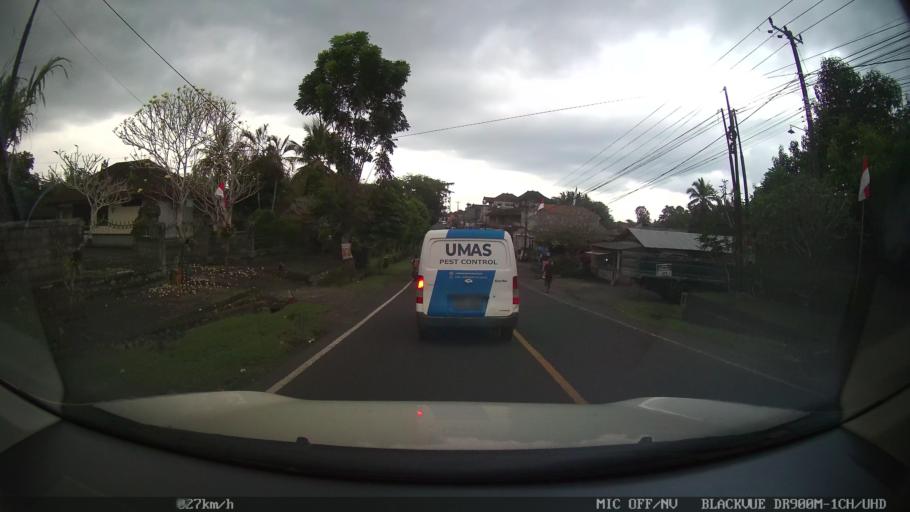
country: ID
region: Bali
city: Banjar Bantasbaleagung
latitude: -8.5023
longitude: 115.0656
